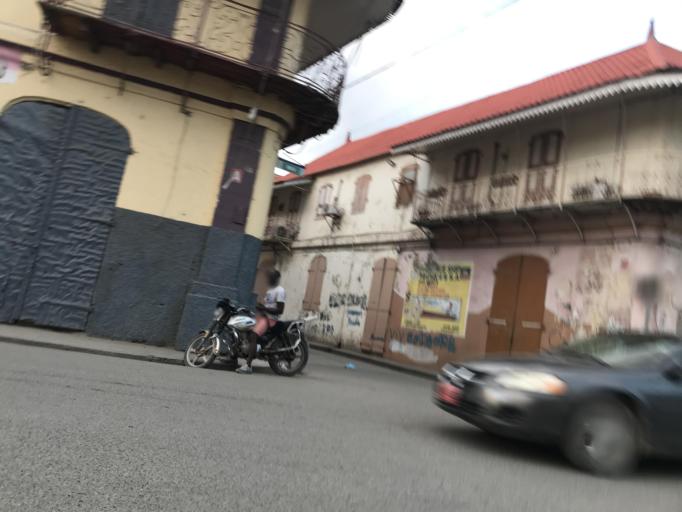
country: HT
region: Nord
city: Okap
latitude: 19.7593
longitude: -72.1993
